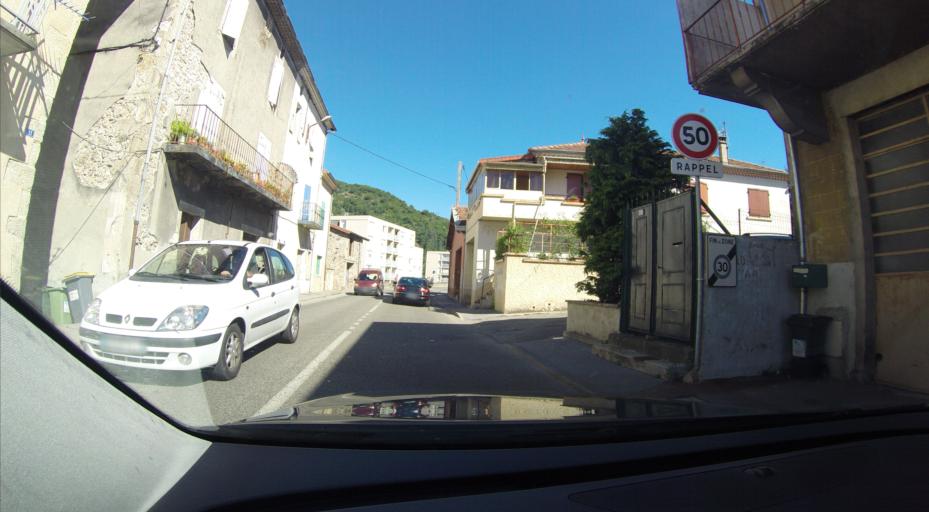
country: FR
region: Rhone-Alpes
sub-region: Departement de l'Ardeche
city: Vals-les-Bains
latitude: 44.6672
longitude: 4.3658
